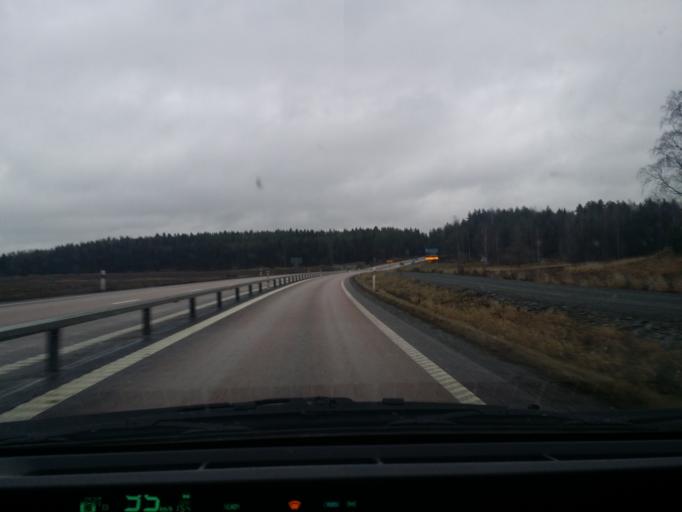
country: SE
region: Vaestmanland
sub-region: Sala Kommun
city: Sala
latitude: 59.8788
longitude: 16.5455
